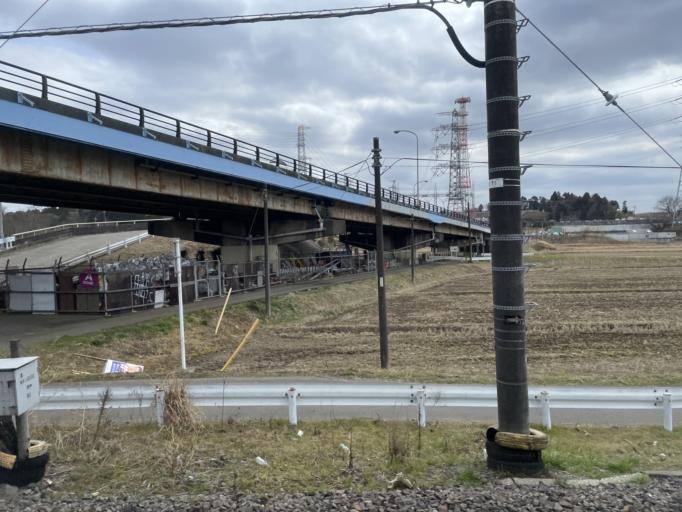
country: JP
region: Chiba
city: Shisui
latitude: 35.7139
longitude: 140.2640
